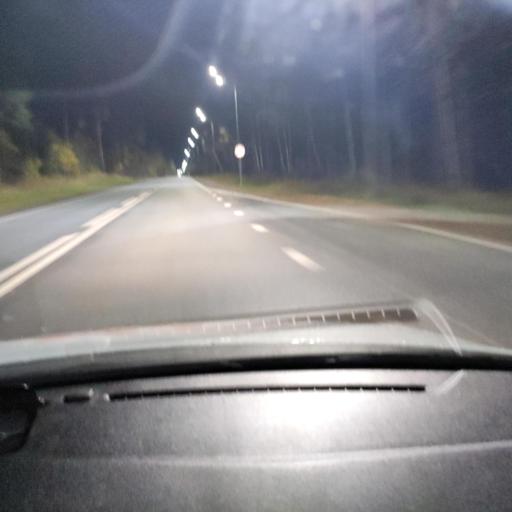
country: RU
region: Tatarstan
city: Stolbishchi
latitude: 55.6362
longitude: 49.0651
